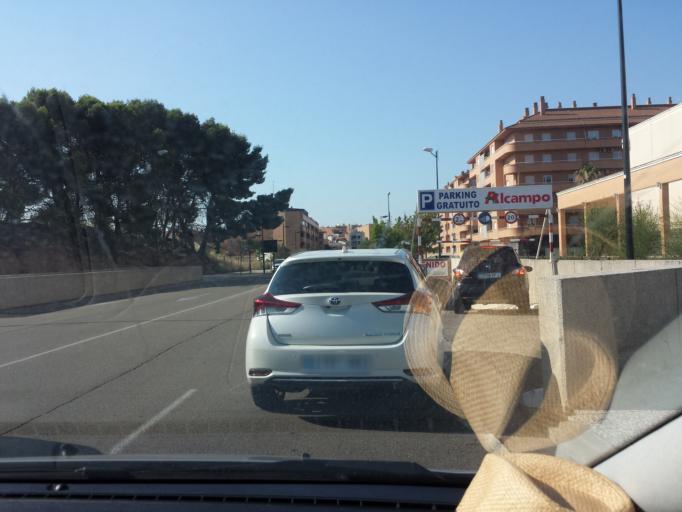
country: ES
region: Aragon
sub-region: Provincia de Zaragoza
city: Oliver-Valdefierro, Oliver, Valdefierro
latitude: 41.6438
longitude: -0.9343
